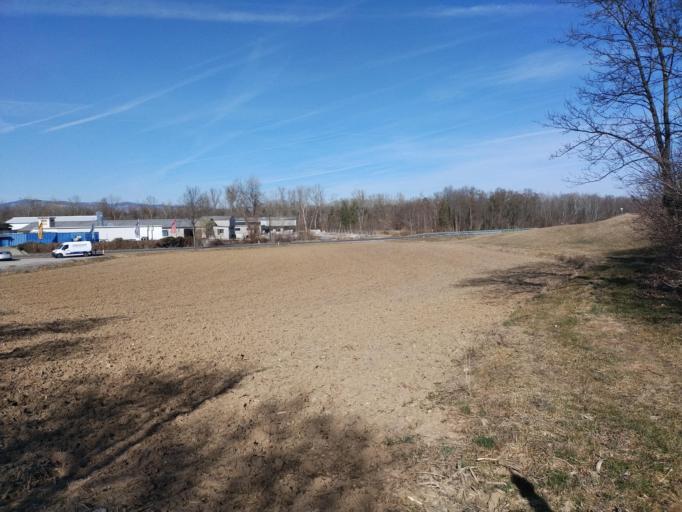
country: AT
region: Lower Austria
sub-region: Politischer Bezirk Neunkirchen
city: Breitenau
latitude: 47.7191
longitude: 16.1545
